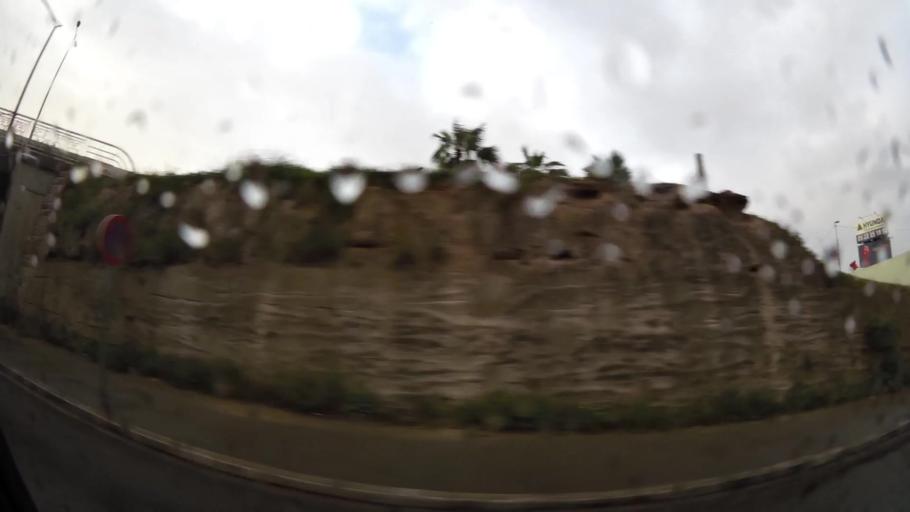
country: MA
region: Grand Casablanca
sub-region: Casablanca
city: Casablanca
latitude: 33.5785
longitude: -7.5551
